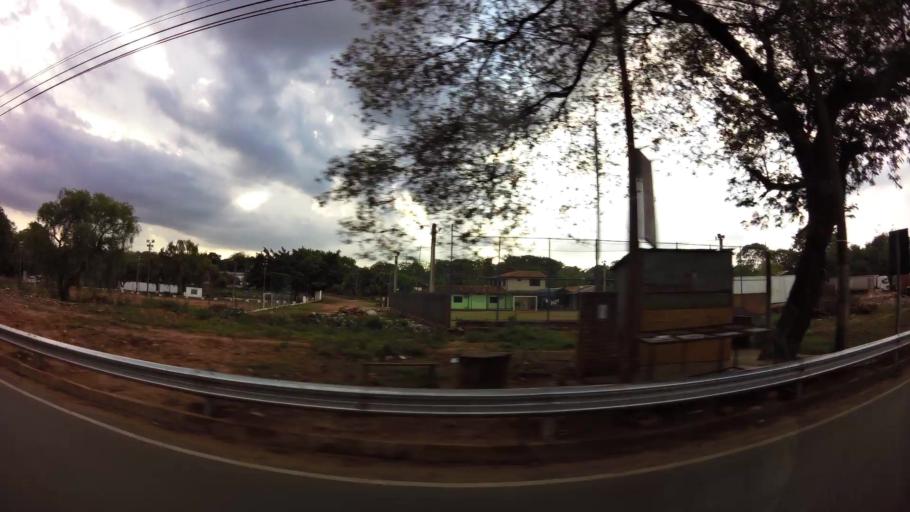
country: PY
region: Central
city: Nemby
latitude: -25.3757
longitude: -57.5447
